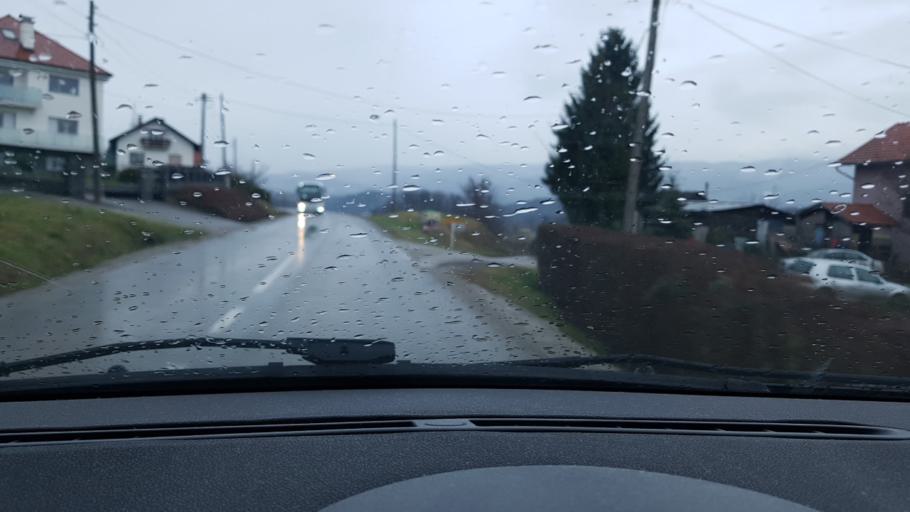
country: HR
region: Krapinsko-Zagorska
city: Oroslavje
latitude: 45.9783
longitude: 15.9054
